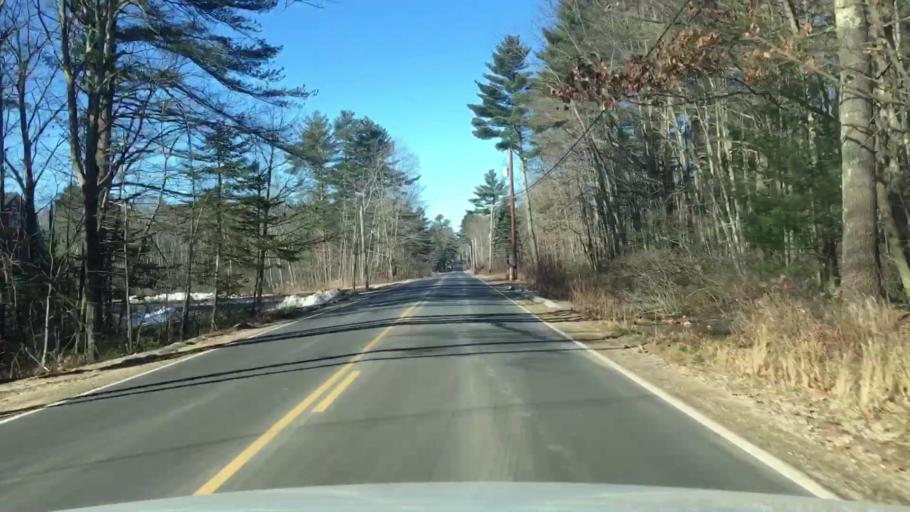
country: US
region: Maine
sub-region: York County
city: Arundel
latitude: 43.4205
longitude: -70.5059
